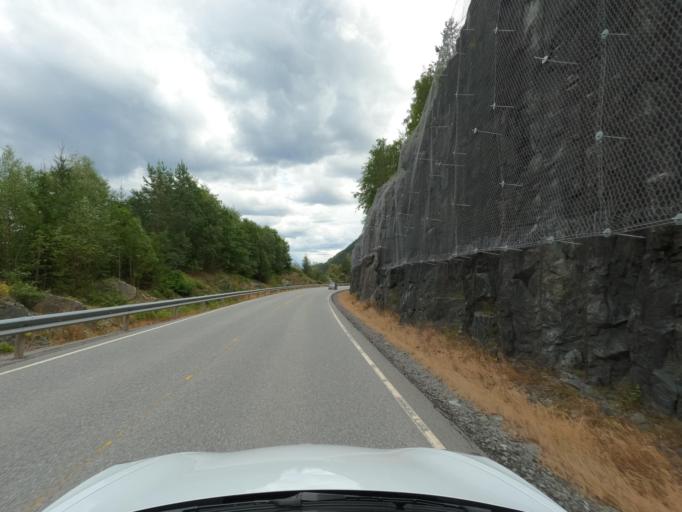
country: NO
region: Telemark
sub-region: Hjartdal
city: Sauland
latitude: 59.8823
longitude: 8.9121
